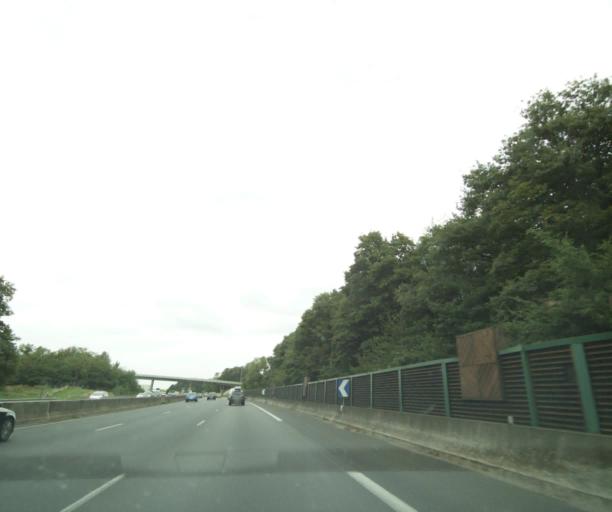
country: FR
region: Centre
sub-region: Departement d'Indre-et-Loire
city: Rochecorbon
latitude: 47.4120
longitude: 0.7282
